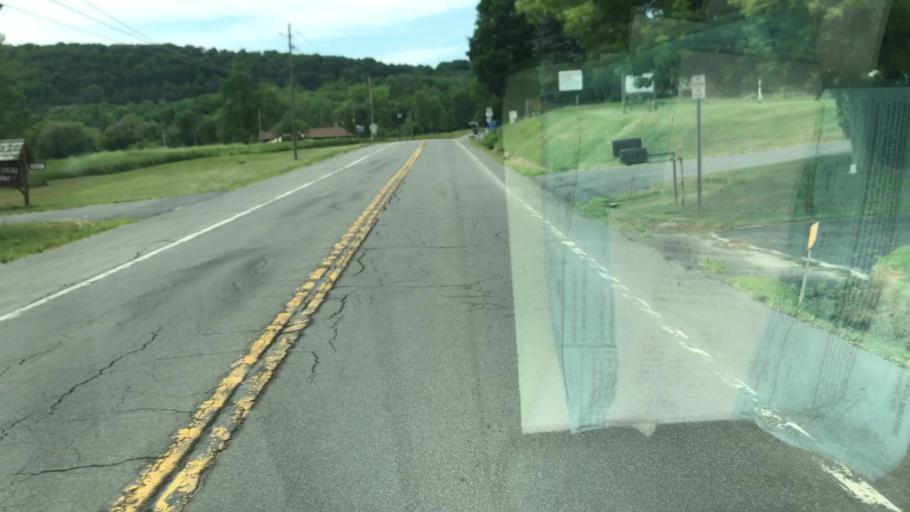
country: US
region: New York
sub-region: Onondaga County
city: Marcellus
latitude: 42.9310
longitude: -76.3321
